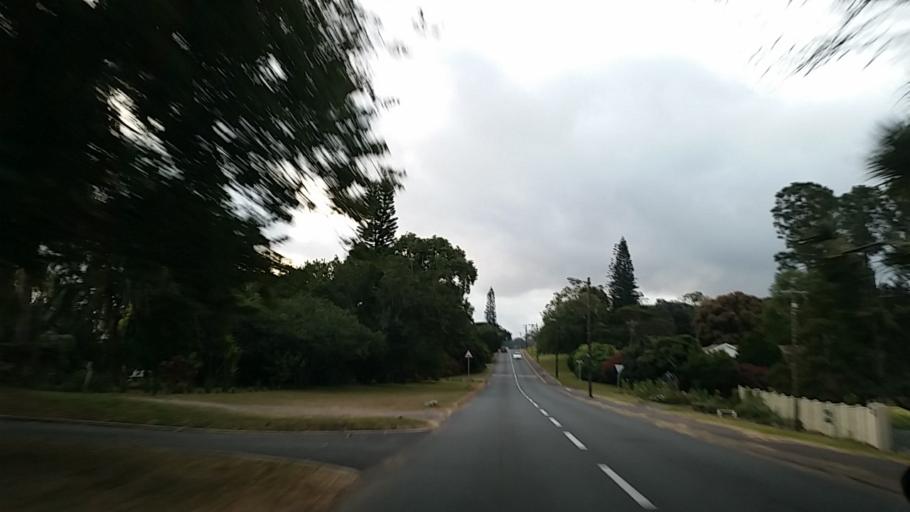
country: ZA
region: KwaZulu-Natal
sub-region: eThekwini Metropolitan Municipality
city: Berea
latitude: -29.8527
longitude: 30.9085
